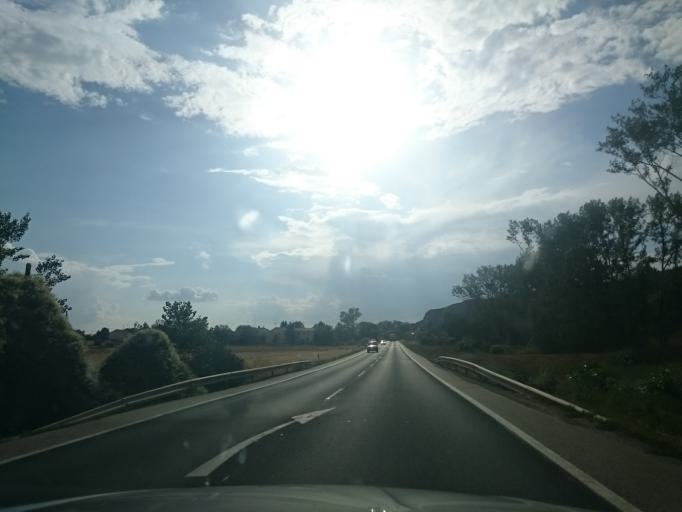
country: ES
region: Castille and Leon
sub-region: Provincia de Burgos
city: Tosantos
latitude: 42.4138
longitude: -3.2374
